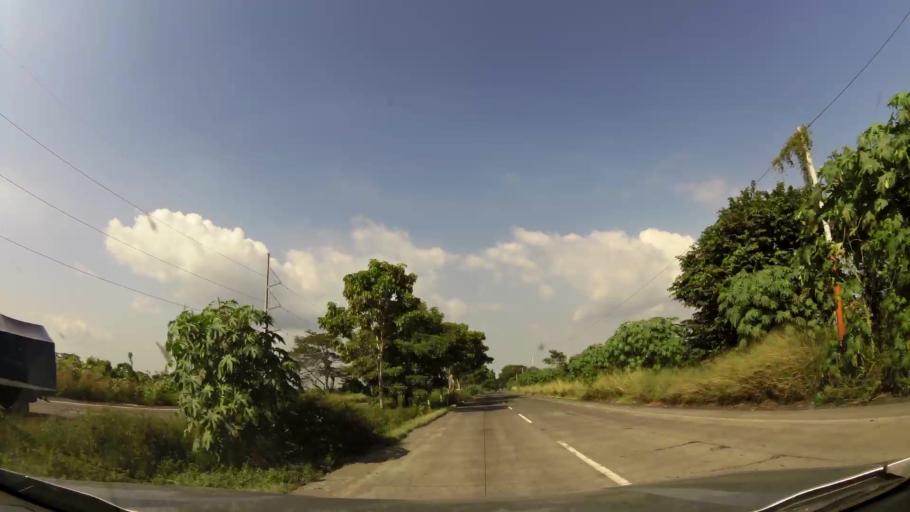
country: GT
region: Escuintla
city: Puerto San Jose
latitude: 13.9991
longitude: -90.7875
